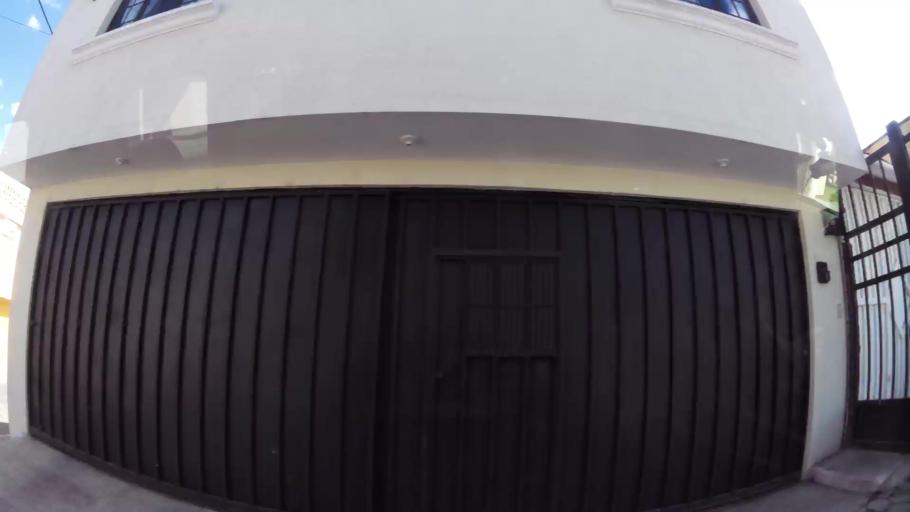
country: GT
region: Quetzaltenango
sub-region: Municipio de La Esperanza
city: La Esperanza
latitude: 14.8506
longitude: -91.5430
